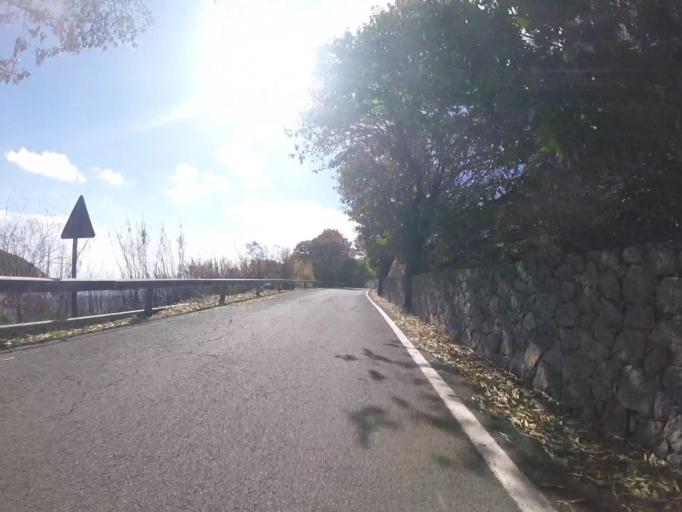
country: ES
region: Canary Islands
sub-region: Provincia de Las Palmas
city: Valleseco
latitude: 28.0114
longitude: -15.5850
